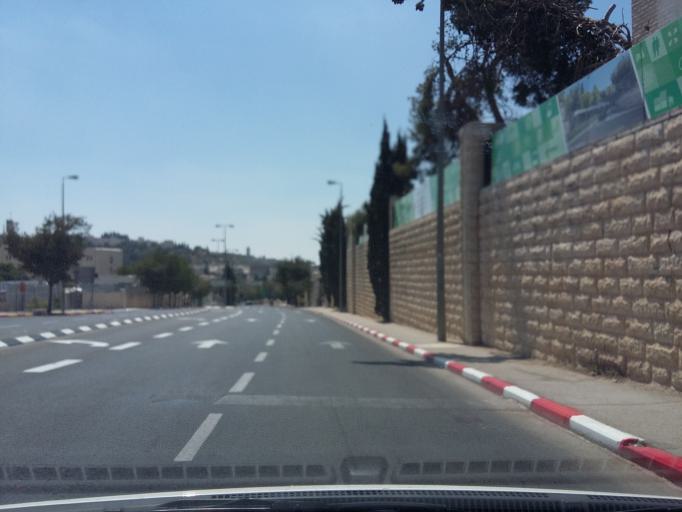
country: PS
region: West Bank
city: East Jerusalem
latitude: 31.7964
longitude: 35.2323
